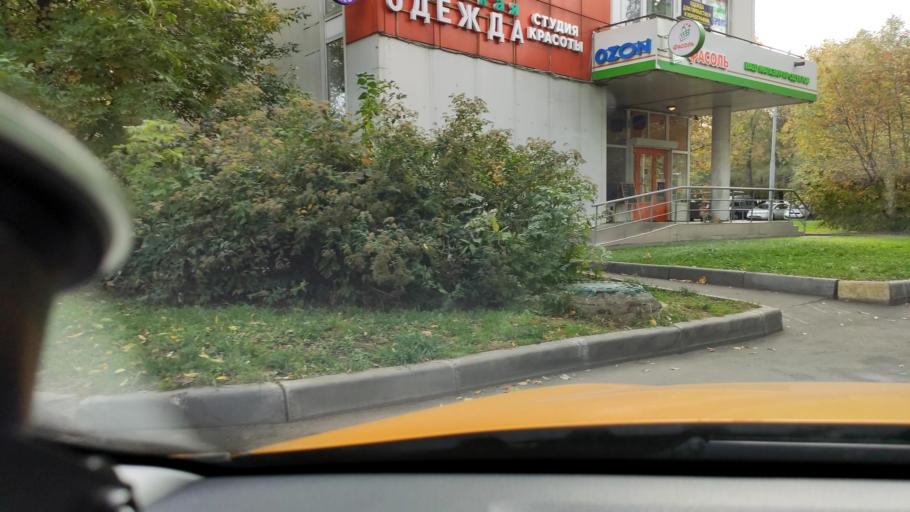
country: RU
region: Moscow
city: Orekhovo-Borisovo
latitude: 55.6247
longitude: 37.7361
